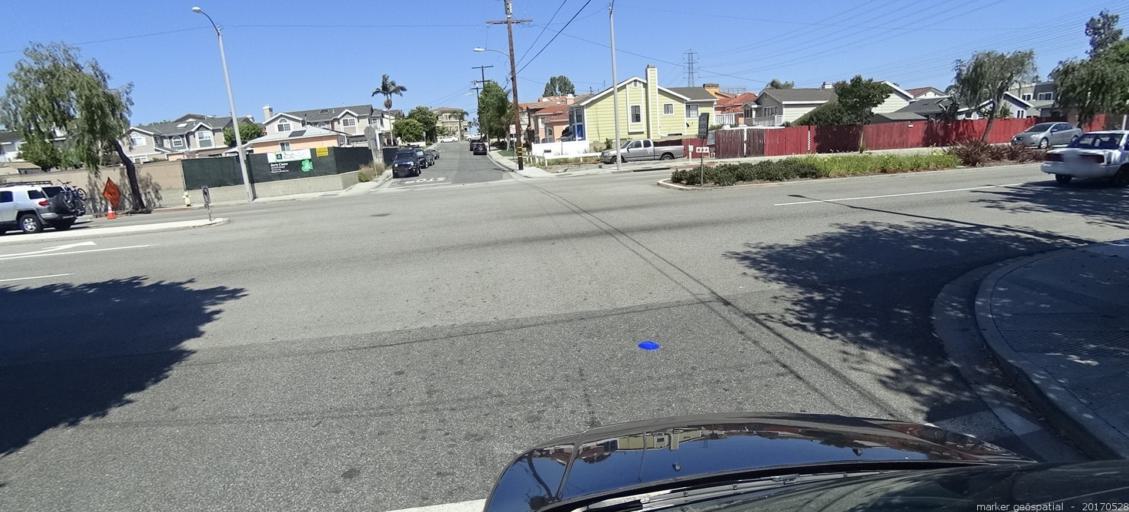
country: US
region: California
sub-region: Los Angeles County
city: Lawndale
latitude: 33.8710
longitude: -118.3615
